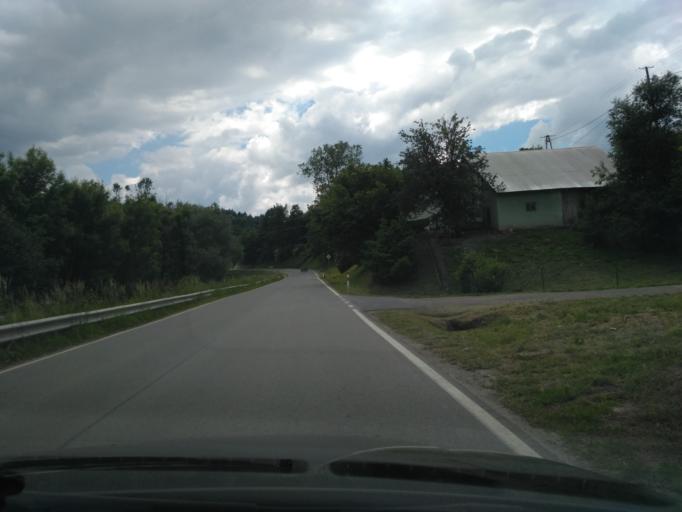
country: PL
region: Subcarpathian Voivodeship
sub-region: Powiat przeworski
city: Jawornik Polski
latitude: 49.8965
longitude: 22.2942
